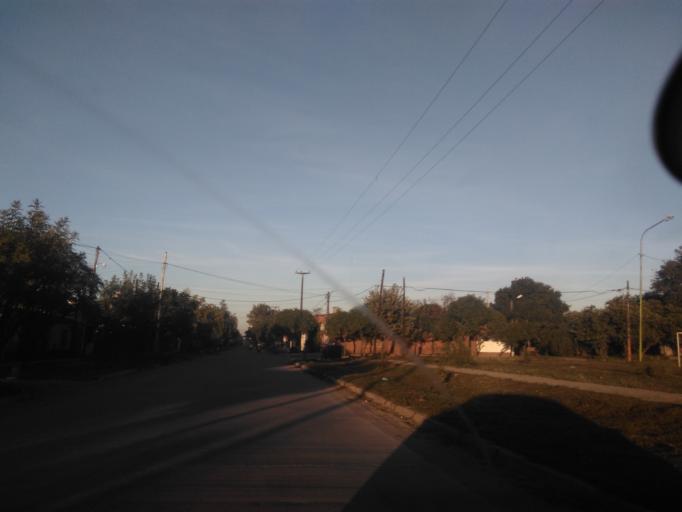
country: AR
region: Chaco
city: Resistencia
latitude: -27.4722
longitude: -58.9869
